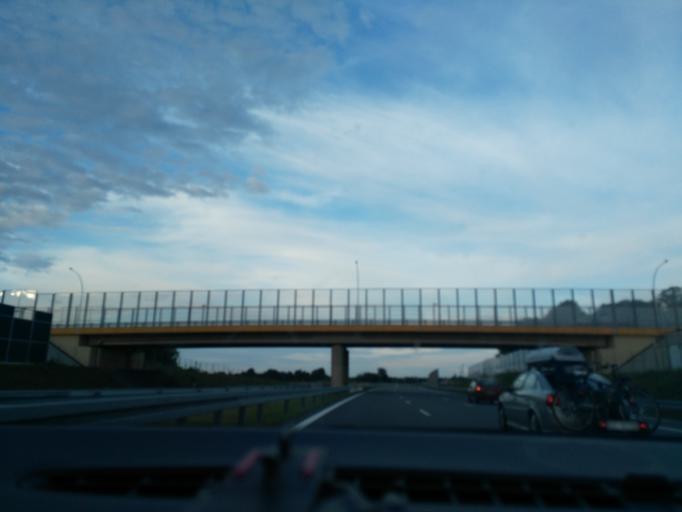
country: PL
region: Lublin Voivodeship
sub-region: Powiat lubelski
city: Jastkow
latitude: 51.3011
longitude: 22.4914
